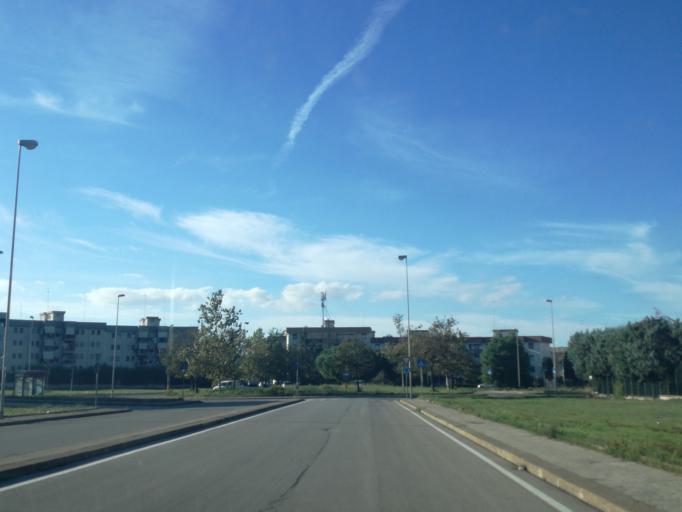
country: IT
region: Apulia
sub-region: Provincia di Bari
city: San Paolo
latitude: 41.1264
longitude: 16.7843
